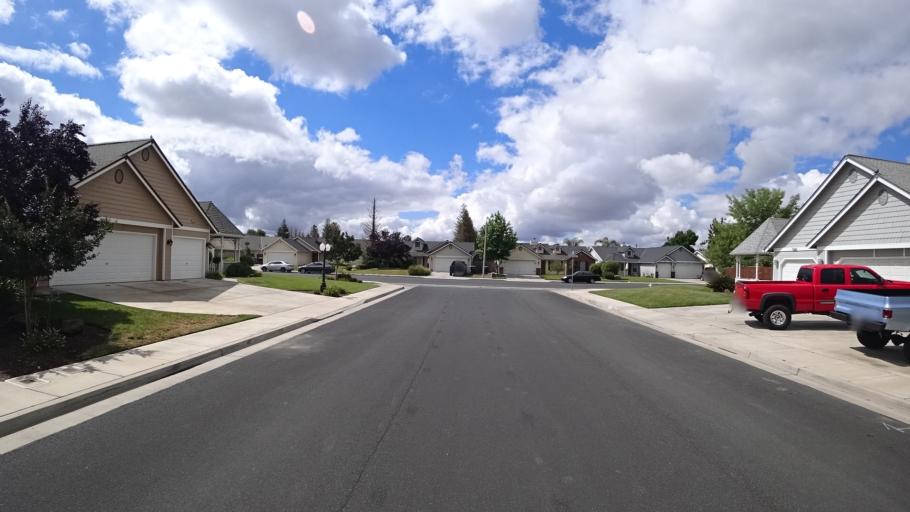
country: US
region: California
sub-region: Kings County
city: Lucerne
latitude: 36.3669
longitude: -119.6568
